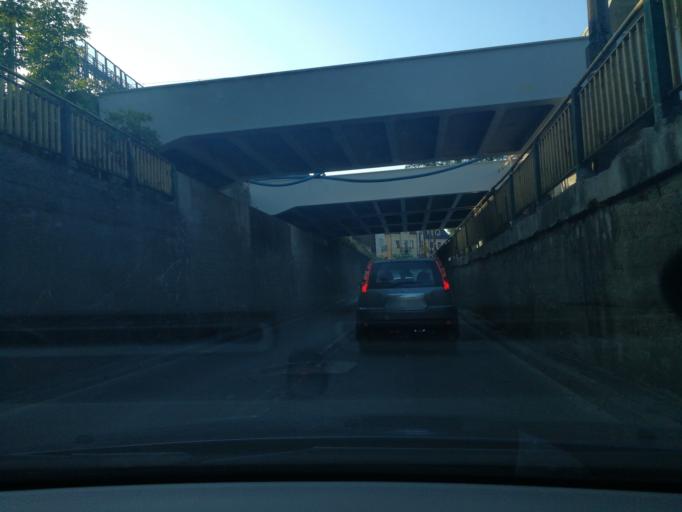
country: PL
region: Masovian Voivodeship
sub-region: Powiat pruszkowski
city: Brwinow
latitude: 52.1413
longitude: 20.7175
